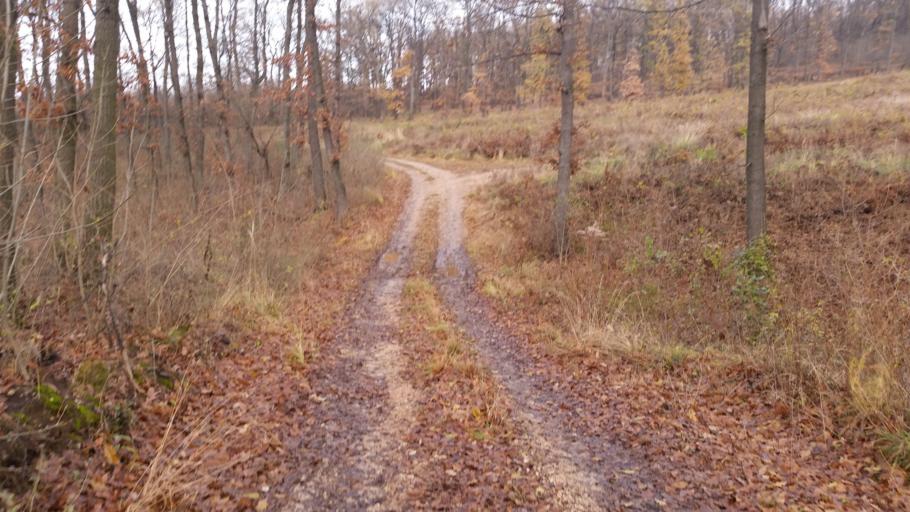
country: HU
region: Pest
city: Telki
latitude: 47.5682
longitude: 18.8194
